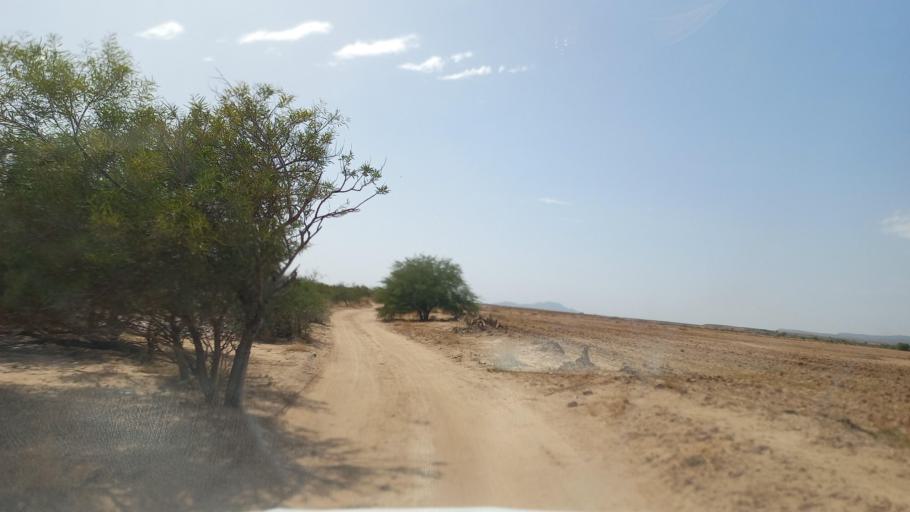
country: TN
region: Al Qasrayn
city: Kasserine
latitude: 35.2568
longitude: 8.9661
